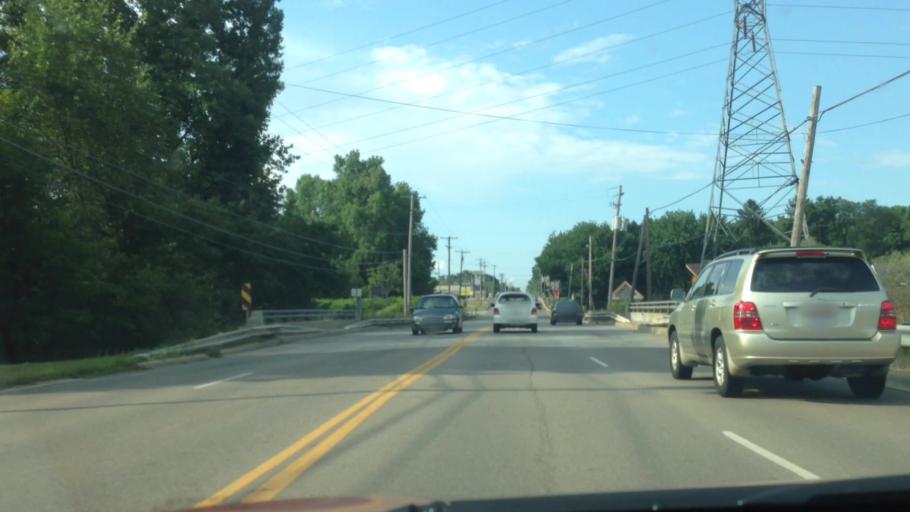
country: US
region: Ohio
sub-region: Summit County
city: Portage Lakes
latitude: 41.0067
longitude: -81.4920
